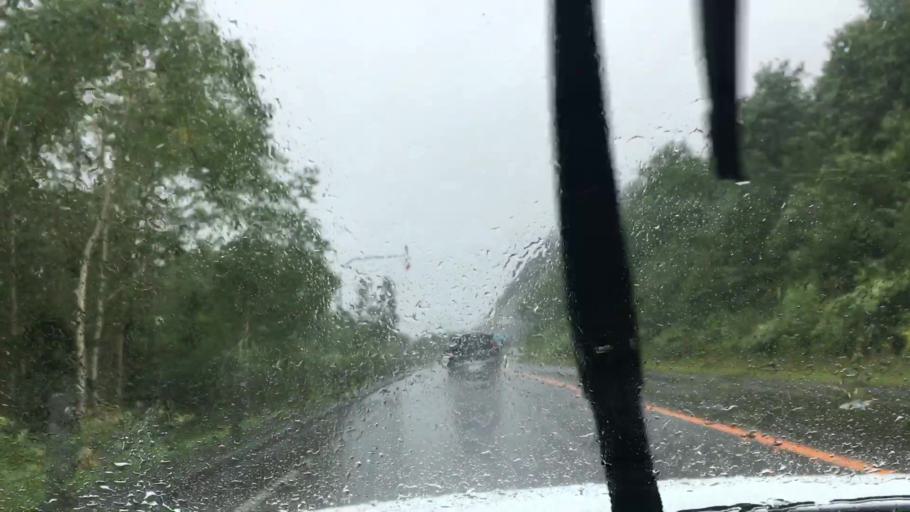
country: JP
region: Hokkaido
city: Sapporo
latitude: 42.8740
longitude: 141.1440
